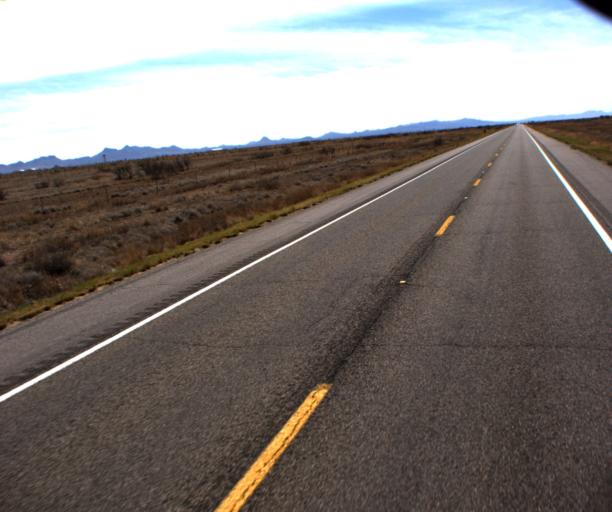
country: US
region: Arizona
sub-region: Cochise County
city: Pirtleville
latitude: 31.4756
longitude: -109.6218
